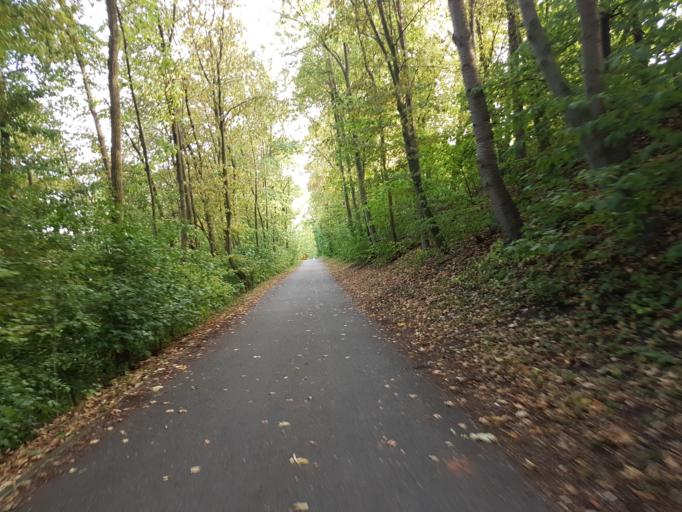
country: DE
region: Lower Saxony
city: Laatzen
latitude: 52.3626
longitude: 9.8616
